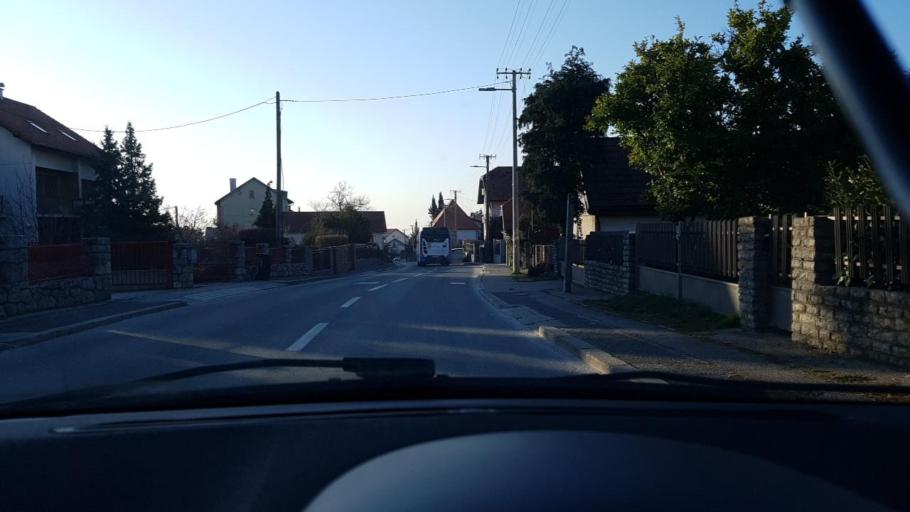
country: HR
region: Grad Zagreb
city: Zagreb
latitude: 45.8431
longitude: 16.0002
